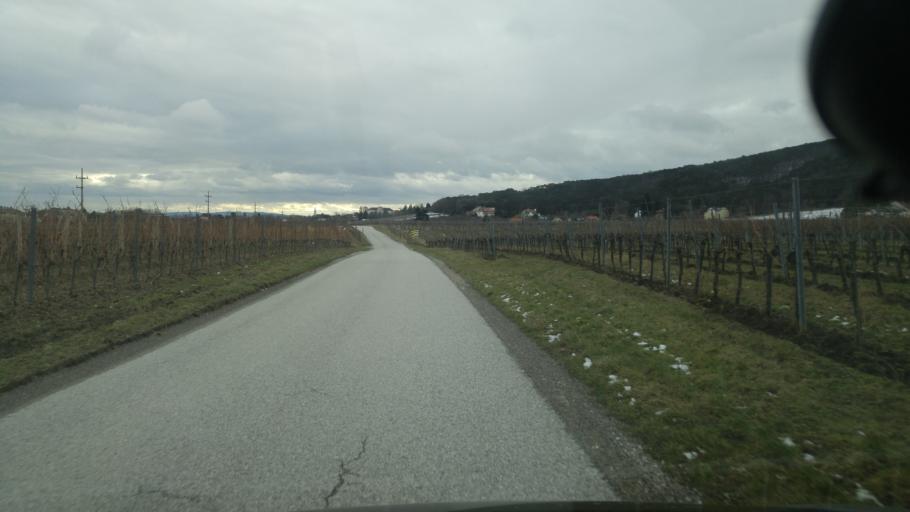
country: AT
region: Lower Austria
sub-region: Politischer Bezirk Baden
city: Bad Voslau
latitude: 47.9804
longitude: 16.2086
